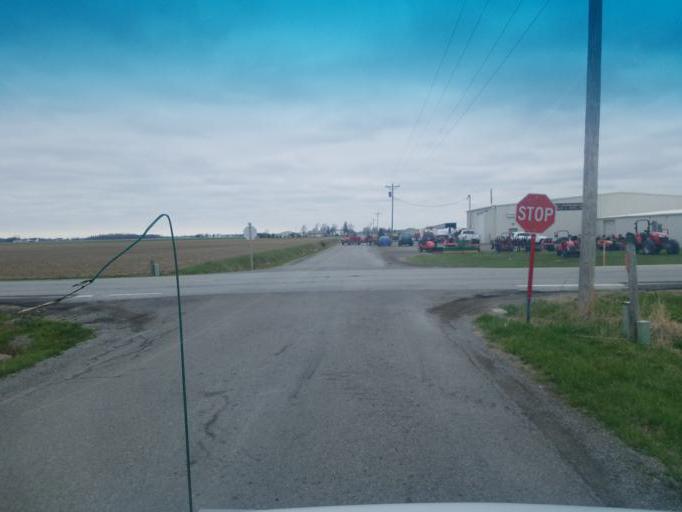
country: US
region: Ohio
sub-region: Allen County
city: Delphos
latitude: 40.9322
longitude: -84.3797
